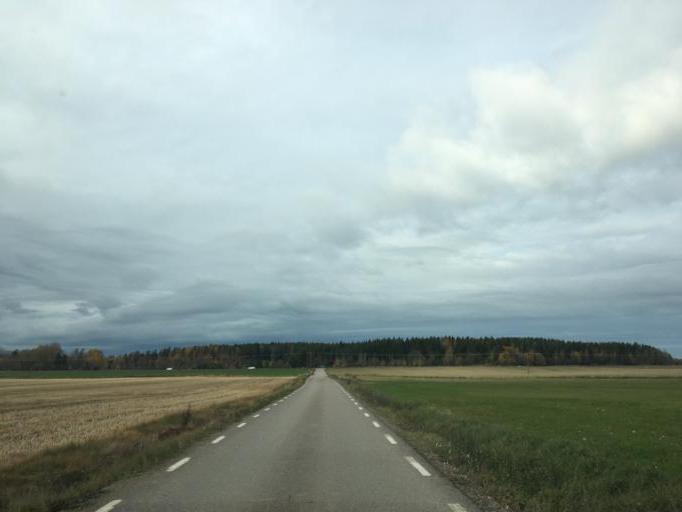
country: SE
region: Vaestmanland
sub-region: Hallstahammars Kommun
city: Kolback
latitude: 59.5499
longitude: 16.3425
